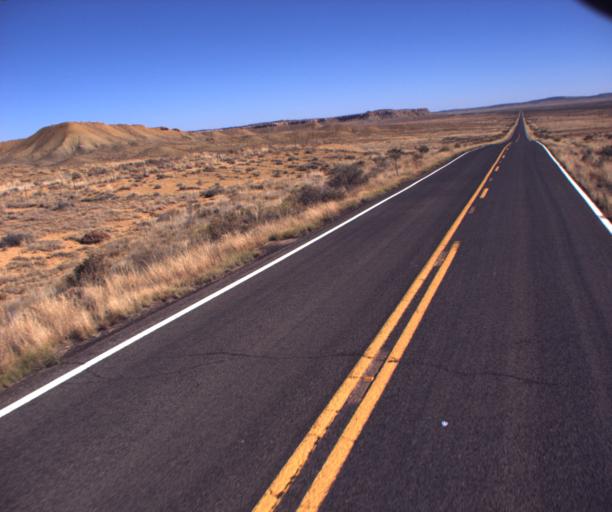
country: US
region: Arizona
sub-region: Navajo County
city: First Mesa
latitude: 35.9765
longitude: -110.7565
